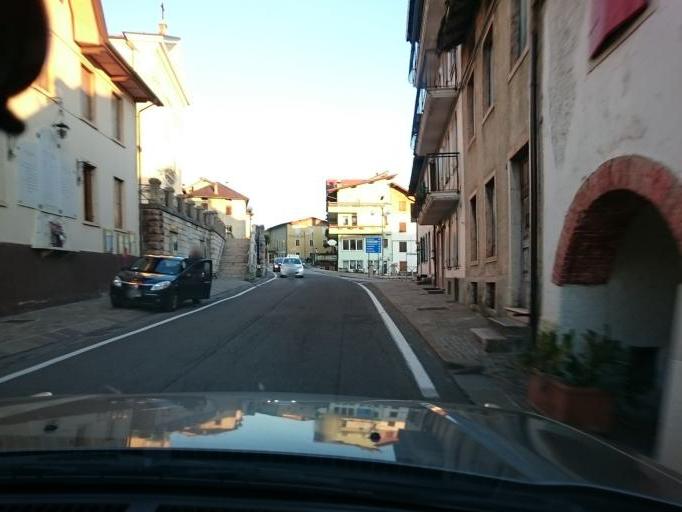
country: IT
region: Veneto
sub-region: Provincia di Vicenza
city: Canove di Roana
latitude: 45.8801
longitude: 11.4852
